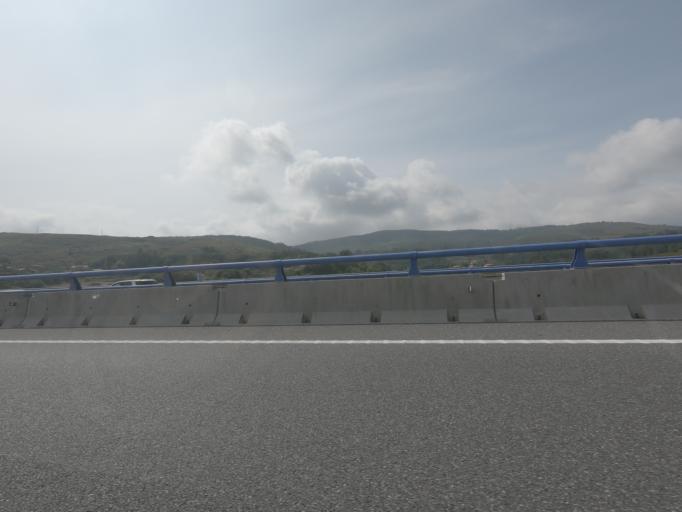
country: ES
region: Galicia
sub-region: Provincia de Pontevedra
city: Covelo
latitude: 42.1956
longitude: -8.3065
